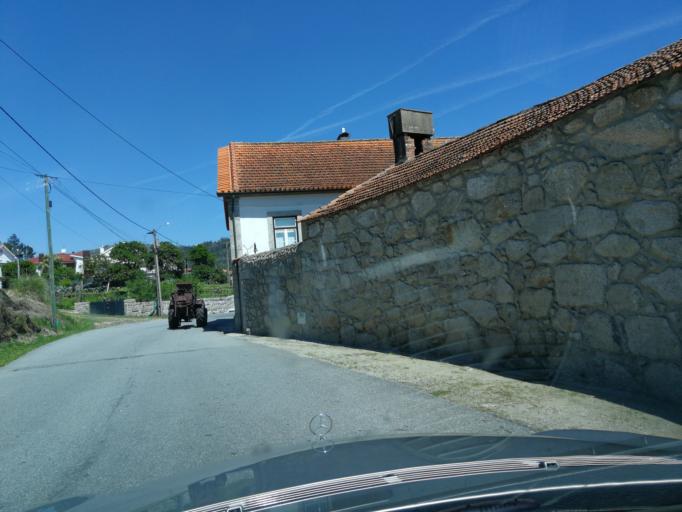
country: PT
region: Viana do Castelo
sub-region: Viana do Castelo
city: Meadela
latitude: 41.7371
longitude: -8.7852
